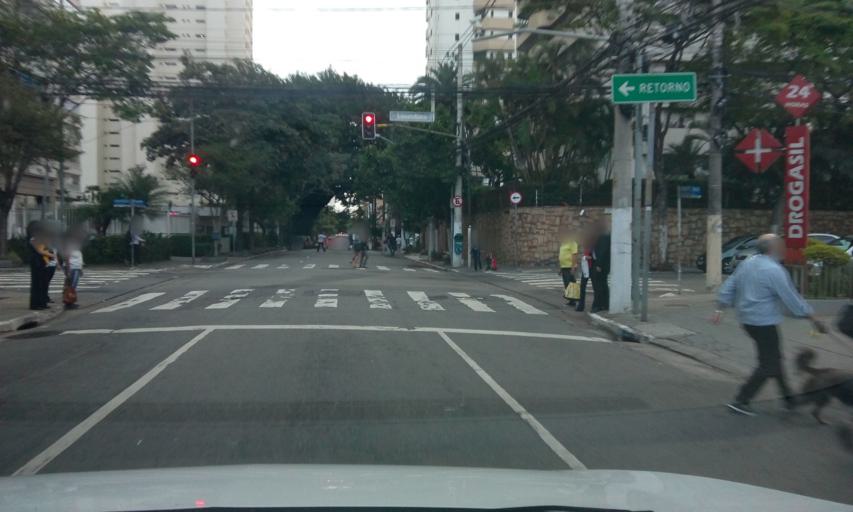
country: BR
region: Sao Paulo
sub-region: Sao Paulo
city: Sao Paulo
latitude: -23.6030
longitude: -46.6636
